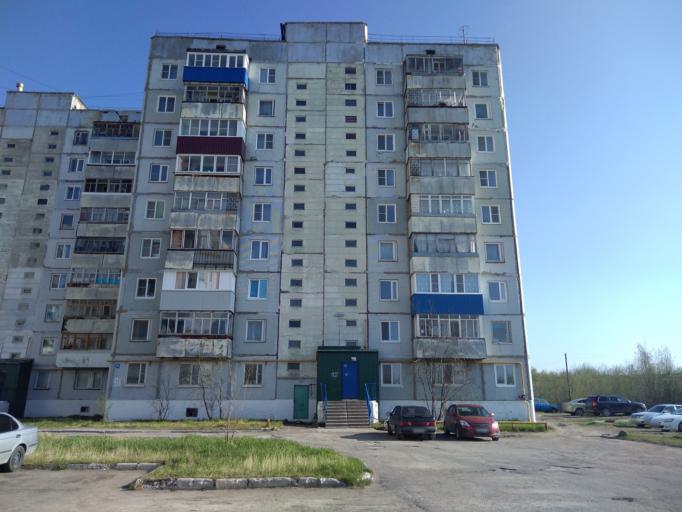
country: RU
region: Komi Republic
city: Pechora
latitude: 65.1375
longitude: 57.1602
